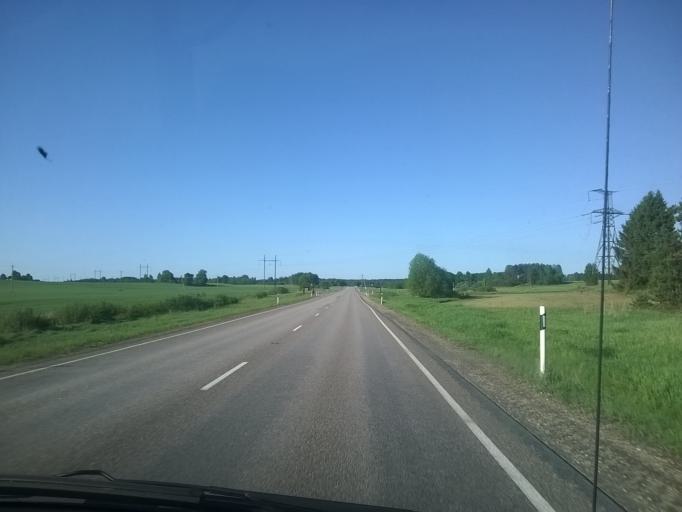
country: EE
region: Valgamaa
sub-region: Torva linn
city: Torva
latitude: 58.0319
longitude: 26.1762
